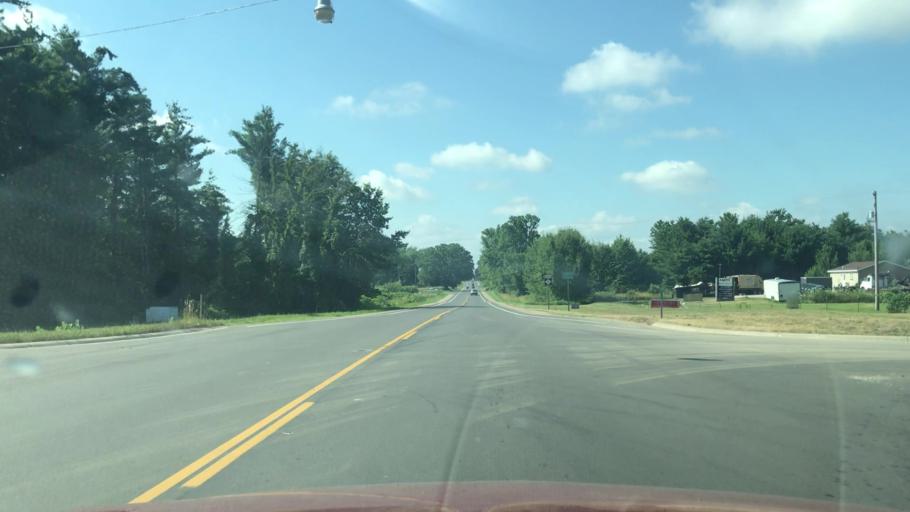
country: US
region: Michigan
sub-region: Newaygo County
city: Newaygo
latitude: 43.3804
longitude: -85.8009
